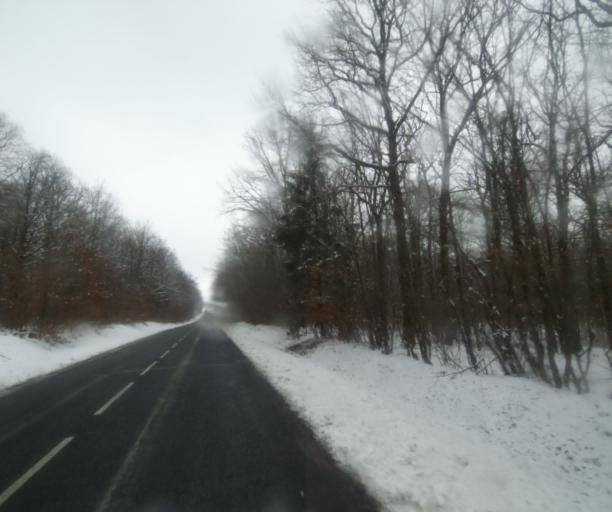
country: FR
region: Champagne-Ardenne
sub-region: Departement de la Haute-Marne
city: Laneuville-a-Remy
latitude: 48.4603
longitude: 4.8976
